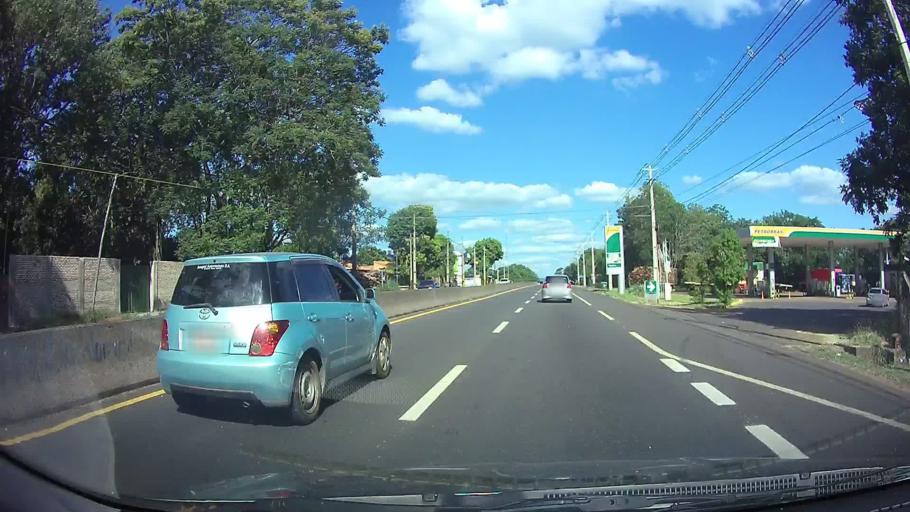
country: PY
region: Central
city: Itaugua
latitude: -25.3998
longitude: -57.3236
